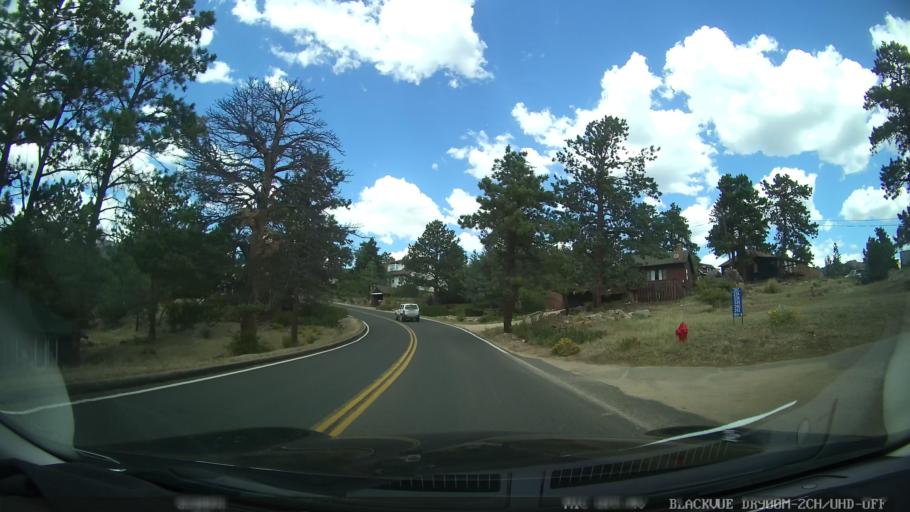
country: US
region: Colorado
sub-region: Larimer County
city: Estes Park
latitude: 40.3778
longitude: -105.5251
